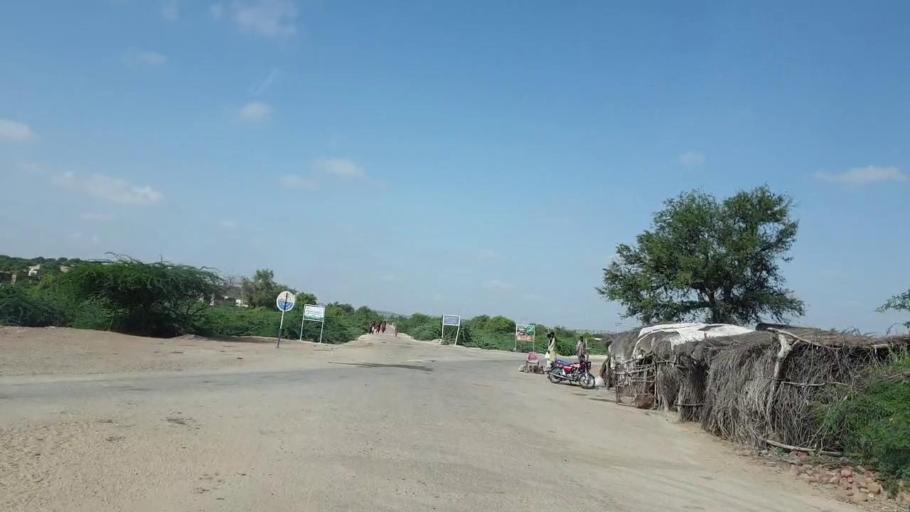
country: PK
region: Sindh
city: Mithi
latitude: 24.5329
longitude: 69.8459
